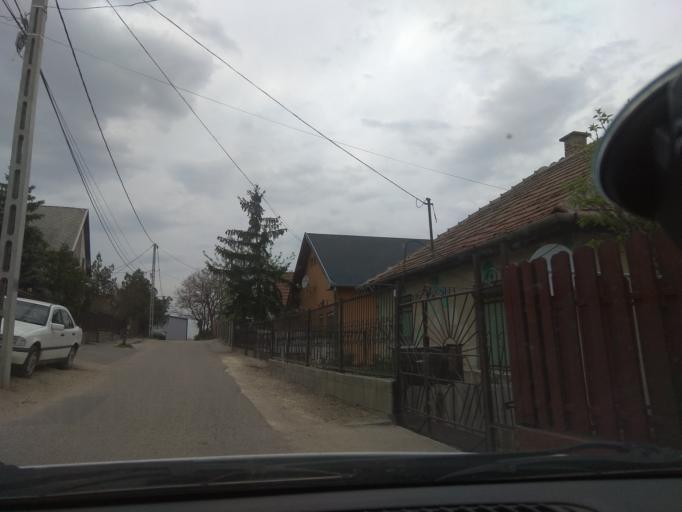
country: HU
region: Pest
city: Halasztelek
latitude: 47.3780
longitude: 19.0110
